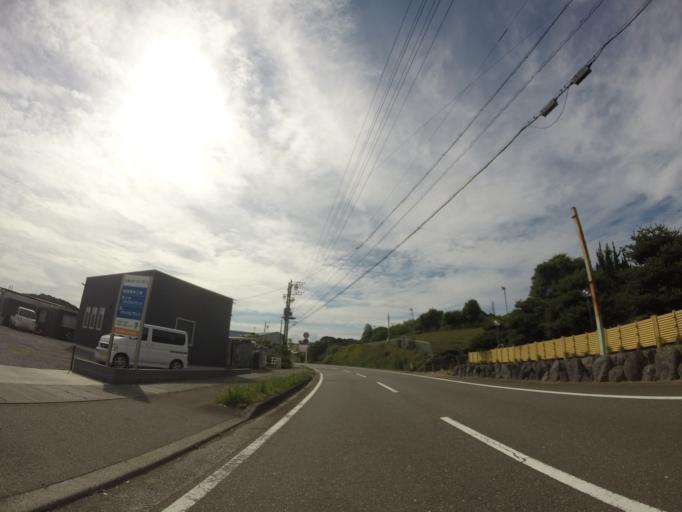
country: JP
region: Shizuoka
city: Shimada
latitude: 34.7616
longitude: 138.2004
